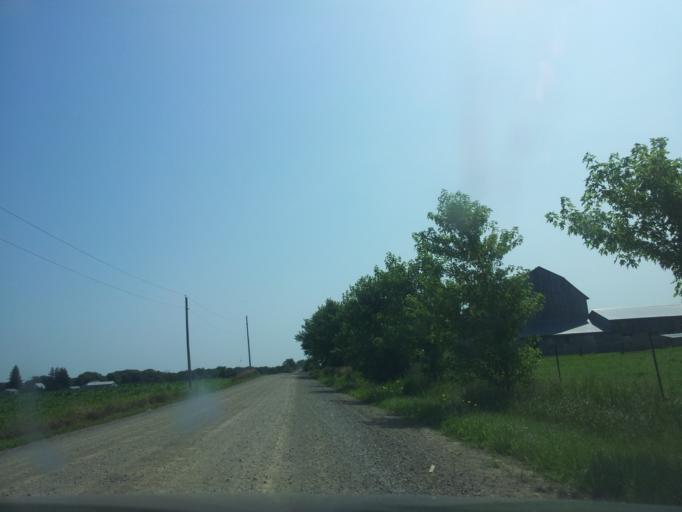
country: CA
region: Ontario
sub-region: Oxford County
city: Woodstock
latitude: 42.9511
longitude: -80.6395
